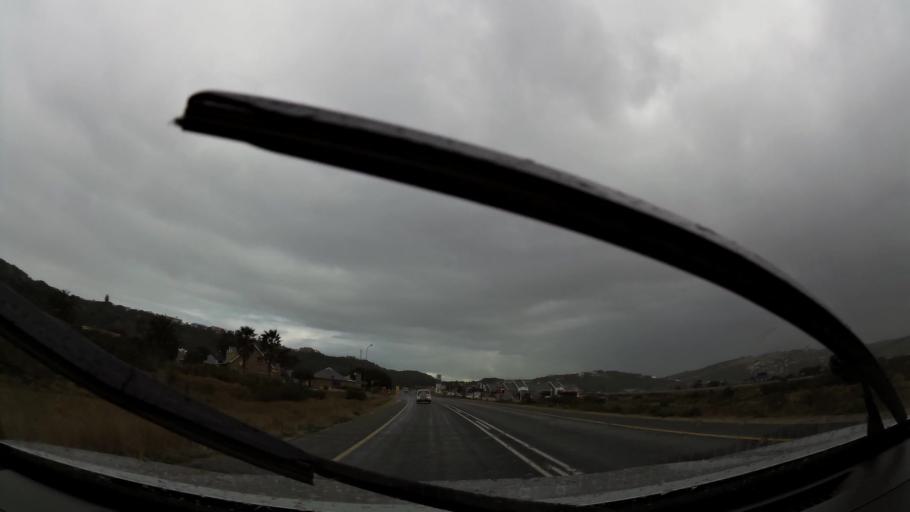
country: ZA
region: Western Cape
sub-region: Eden District Municipality
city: Mossel Bay
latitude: -34.0528
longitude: 22.2279
